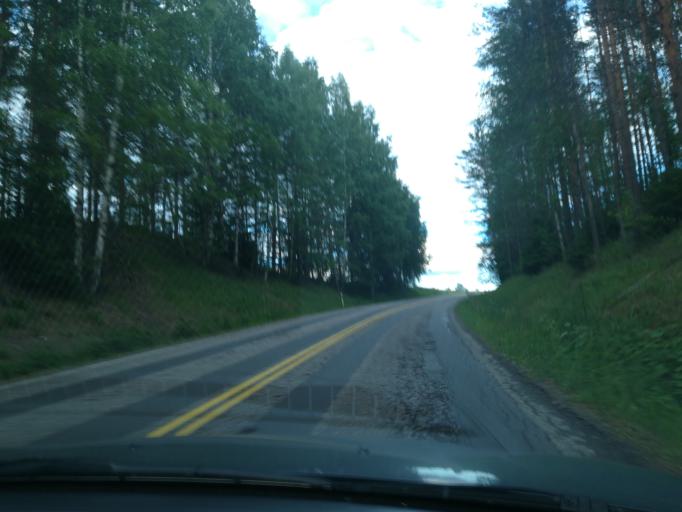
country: FI
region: Southern Savonia
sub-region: Mikkeli
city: Puumala
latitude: 61.5689
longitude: 28.0698
